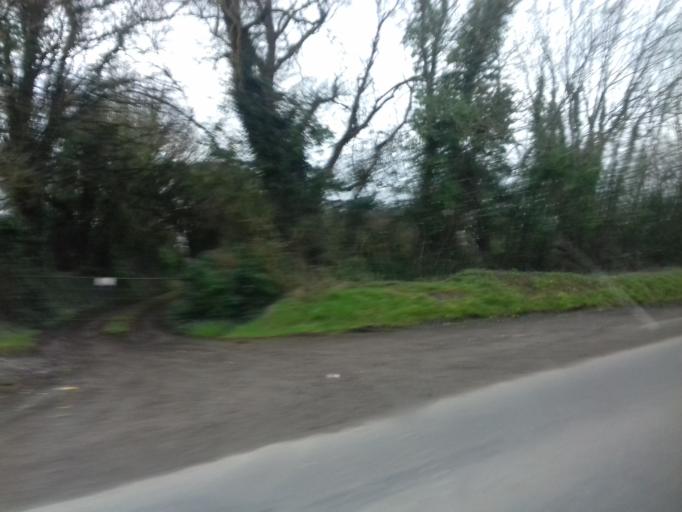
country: IE
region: Leinster
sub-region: An Mhi
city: Duleek
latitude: 53.6964
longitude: -6.4032
